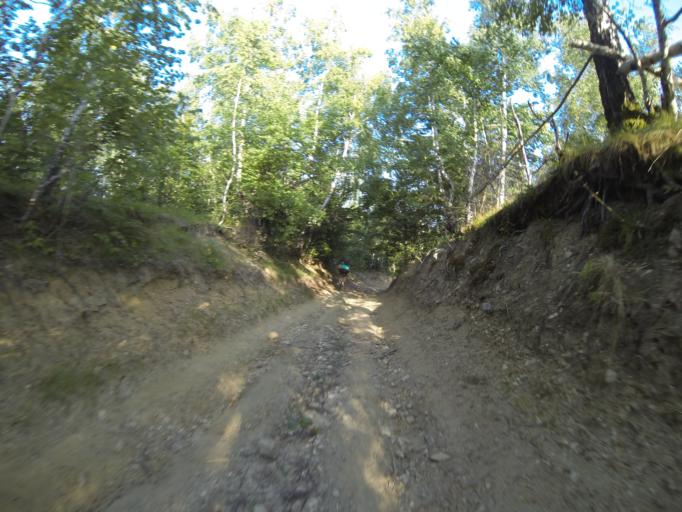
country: RO
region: Valcea
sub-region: Comuna Costesti
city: Bistrita
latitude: 45.1991
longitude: 23.9833
